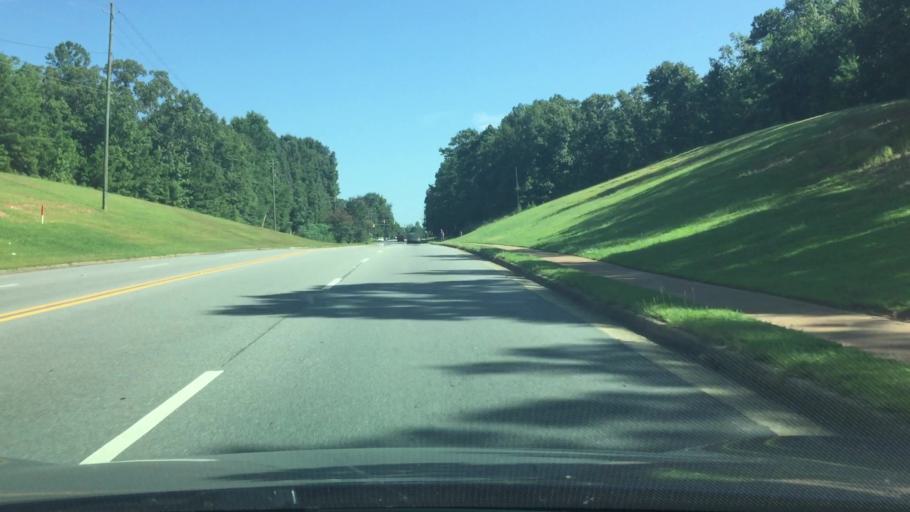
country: US
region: Alabama
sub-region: Lee County
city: Auburn
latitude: 32.6147
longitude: -85.4476
